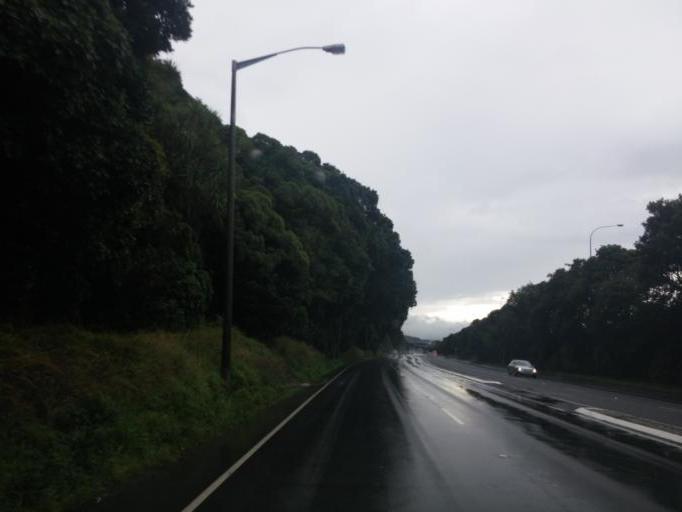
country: NZ
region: Wellington
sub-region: Wellington City
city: Wellington
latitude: -41.2515
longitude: 174.8066
